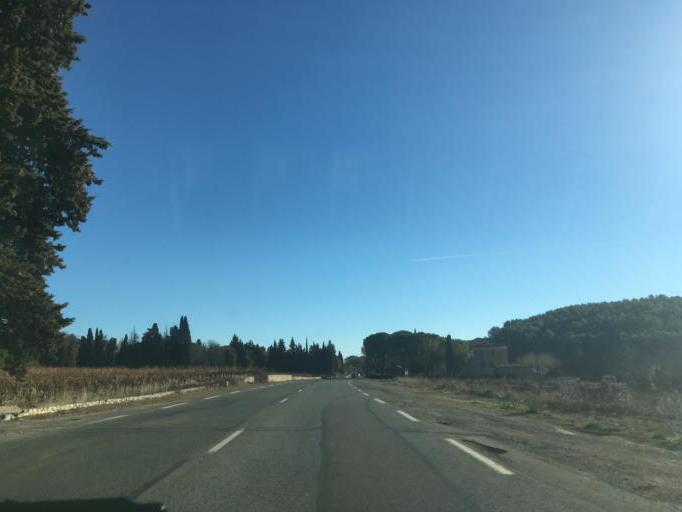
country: FR
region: Provence-Alpes-Cote d'Azur
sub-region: Departement du Var
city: Flayosc
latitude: 43.5406
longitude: 6.3758
